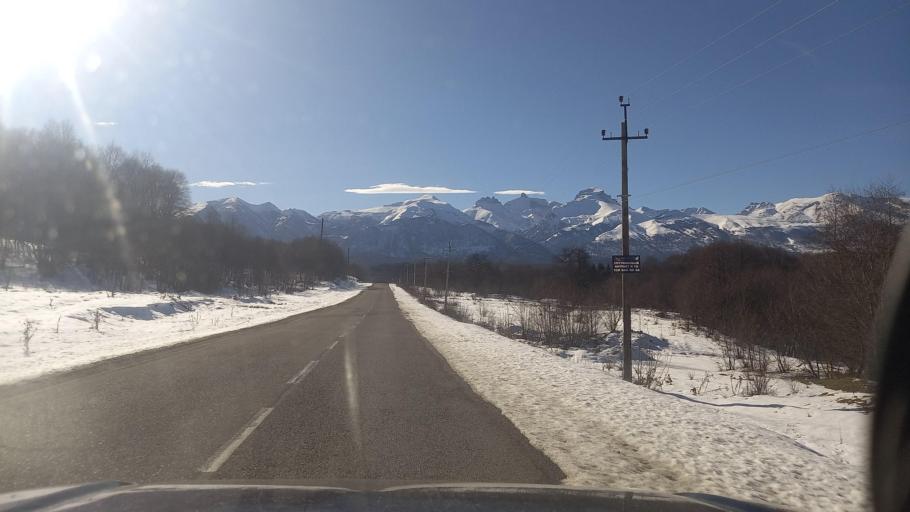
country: RU
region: North Ossetia
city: Chikola
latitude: 43.1258
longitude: 43.8177
